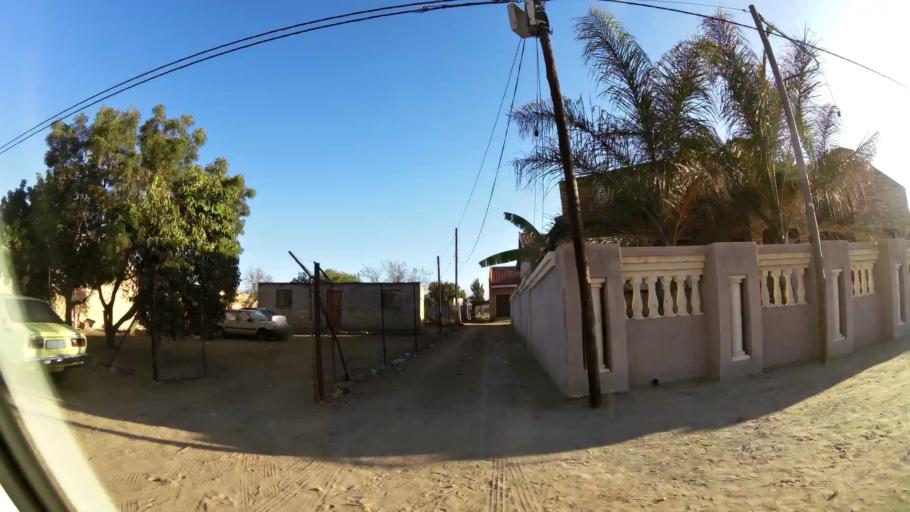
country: ZA
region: Limpopo
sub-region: Capricorn District Municipality
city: Polokwane
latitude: -23.8398
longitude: 29.3624
